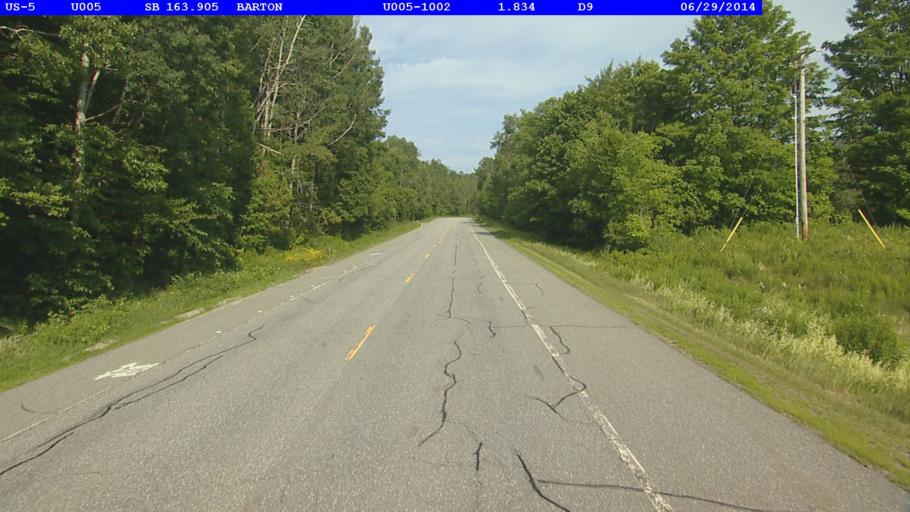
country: US
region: Vermont
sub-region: Caledonia County
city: Lyndonville
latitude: 44.7129
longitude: -72.1268
